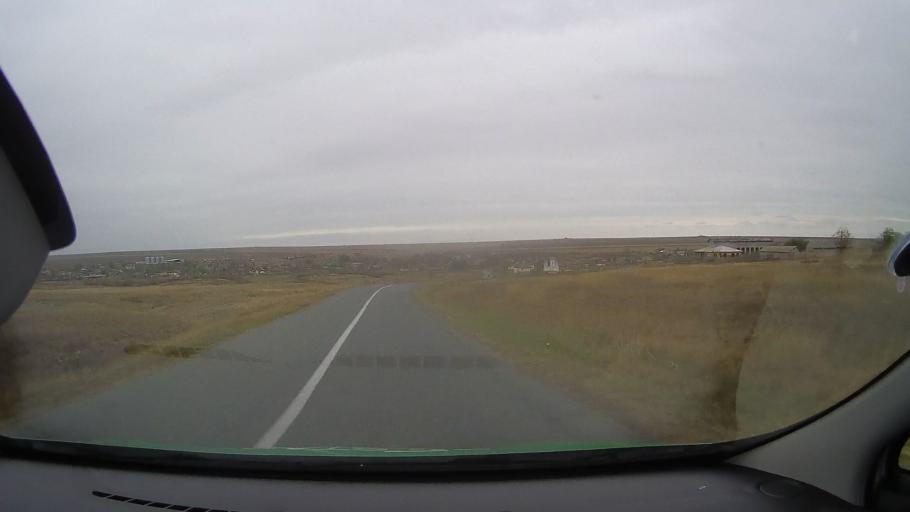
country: RO
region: Constanta
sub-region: Comuna Pantelimon
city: Pantelimon
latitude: 44.5951
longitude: 28.3251
